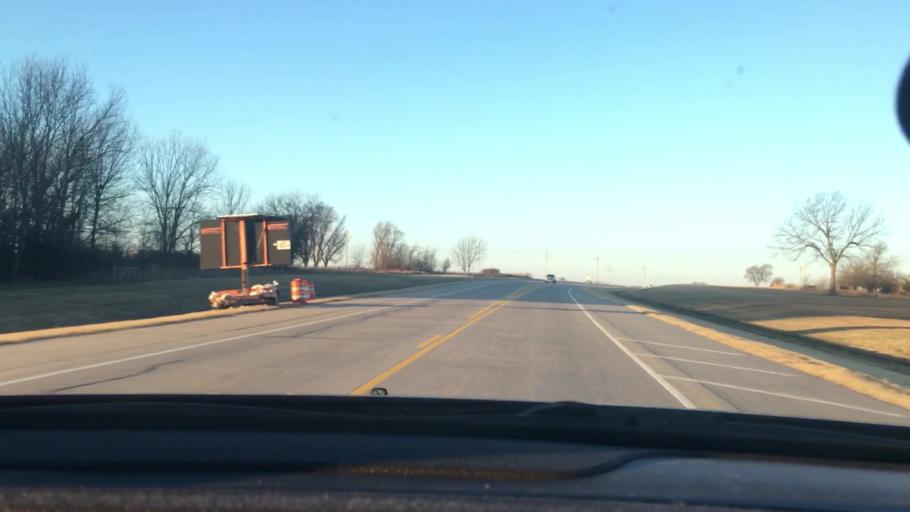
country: US
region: Oklahoma
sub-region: Pontotoc County
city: Ada
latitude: 34.6527
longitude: -96.8056
